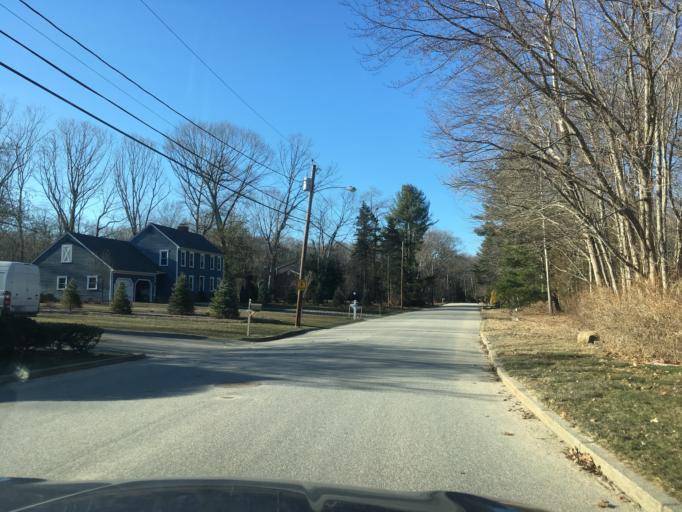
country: US
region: Rhode Island
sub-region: Kent County
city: East Greenwich
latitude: 41.6507
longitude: -71.4921
